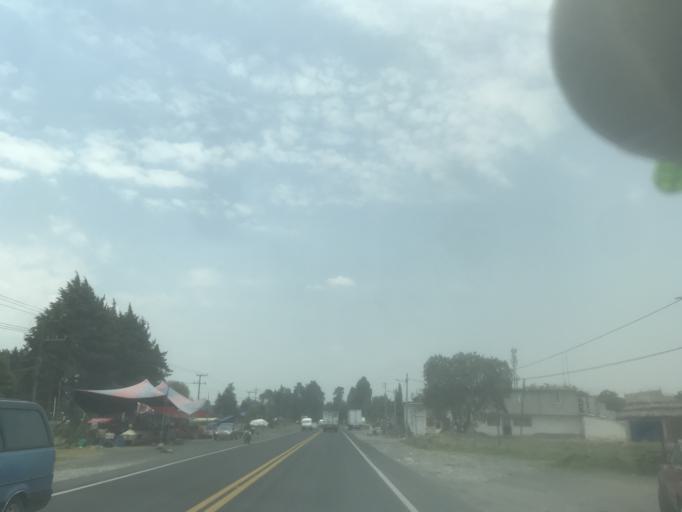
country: MX
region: Mexico
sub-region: Amecameca
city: San Diego Huehuecalco
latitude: 19.0852
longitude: -98.7820
